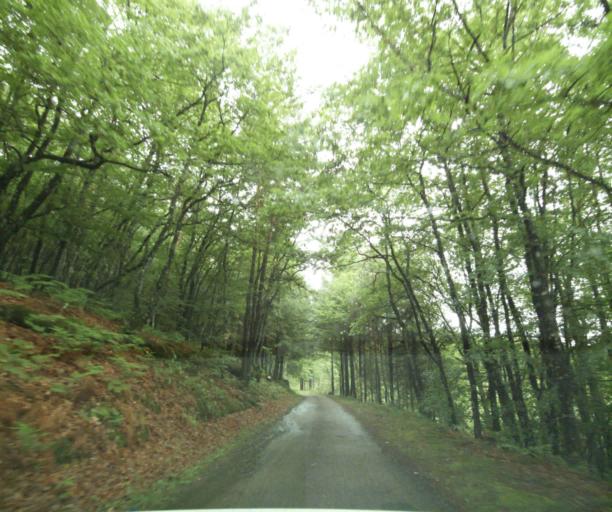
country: FR
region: Bourgogne
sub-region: Departement de Saone-et-Loire
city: Matour
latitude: 46.4454
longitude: 4.4681
